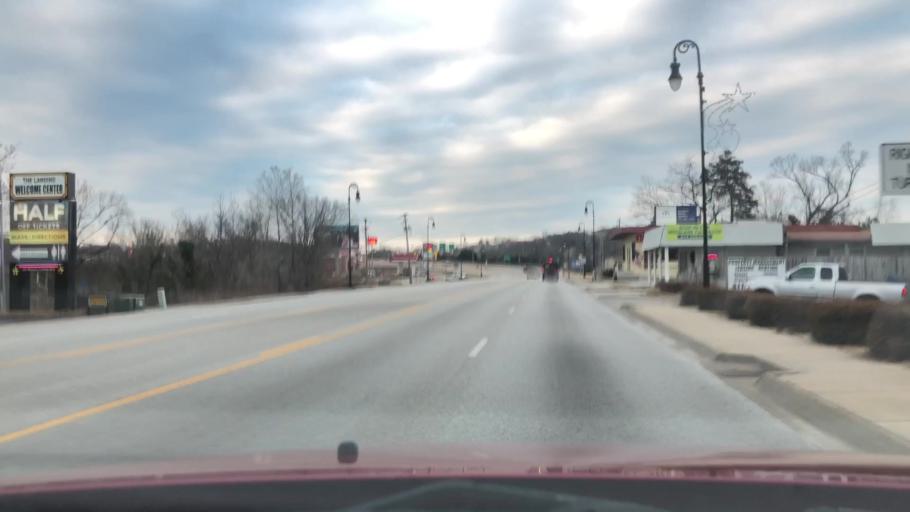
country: US
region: Missouri
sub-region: Taney County
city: Branson
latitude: 36.6532
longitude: -93.2203
